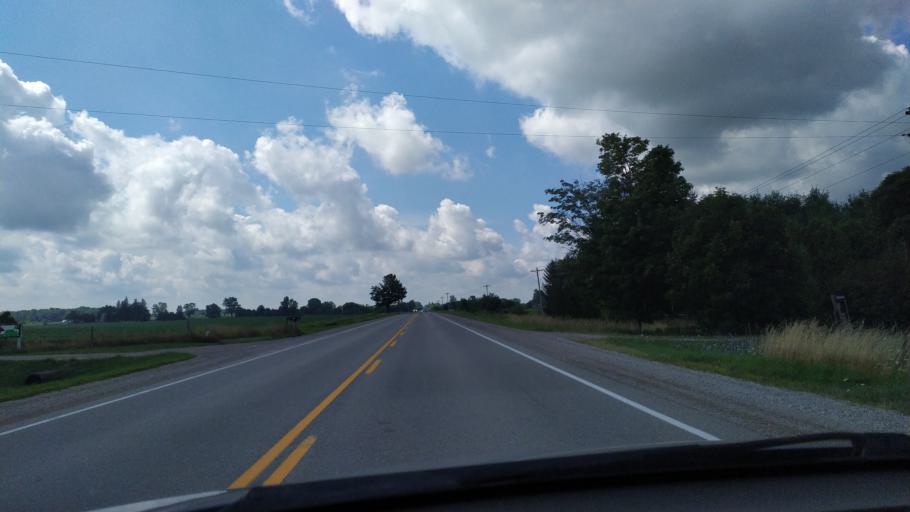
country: CA
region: Ontario
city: South Huron
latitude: 43.3464
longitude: -81.2949
